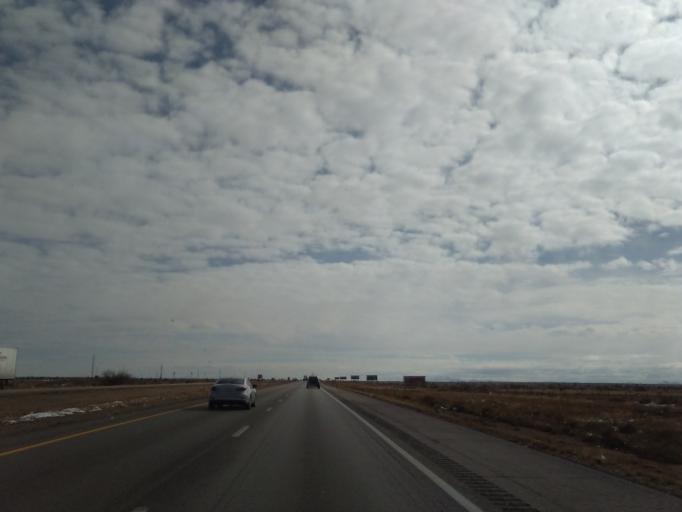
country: US
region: New Mexico
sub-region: Hidalgo County
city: Lordsburg
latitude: 32.2380
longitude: -108.4829
